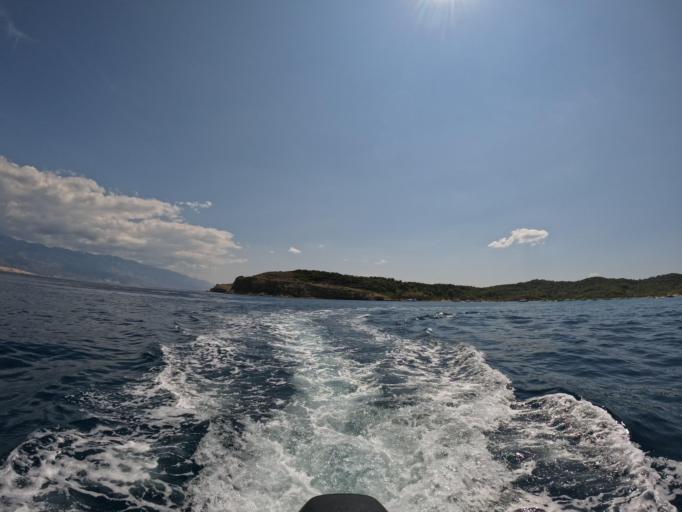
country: HR
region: Primorsko-Goranska
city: Lopar
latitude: 44.8458
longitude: 14.7567
